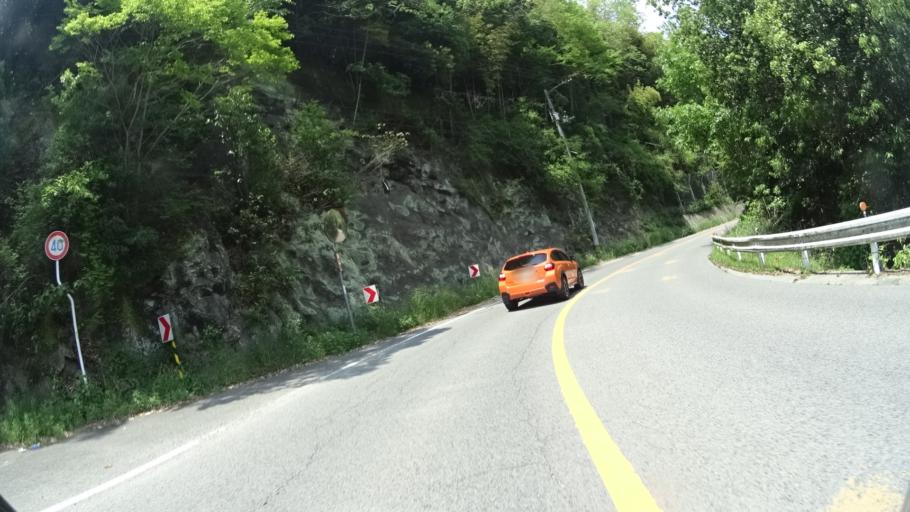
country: JP
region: Ehime
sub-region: Shikoku-chuo Shi
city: Matsuyama
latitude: 33.8829
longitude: 132.8353
